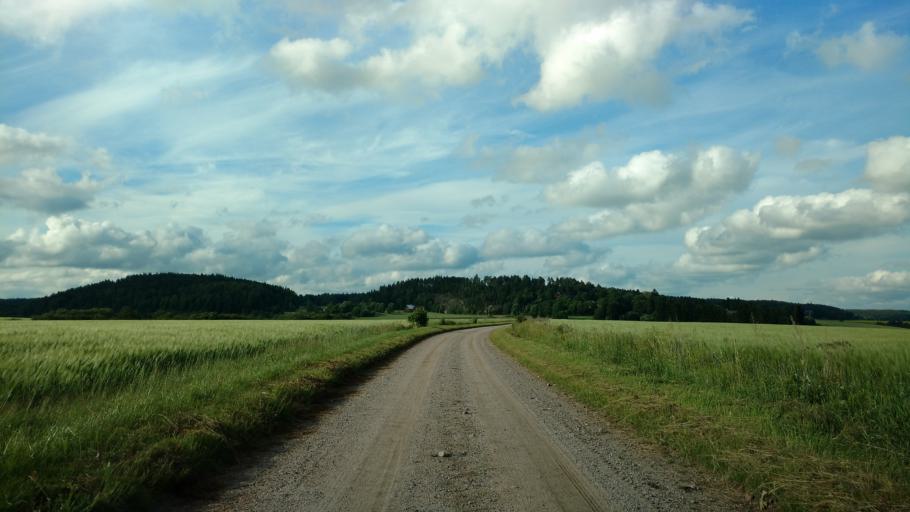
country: FI
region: Varsinais-Suomi
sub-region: Salo
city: Salo
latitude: 60.4188
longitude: 23.1732
